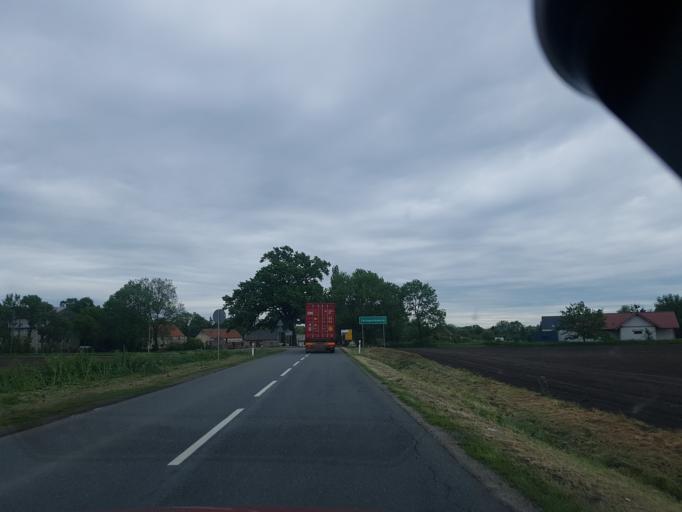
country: PL
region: Lower Silesian Voivodeship
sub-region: Powiat wroclawski
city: Kobierzyce
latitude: 50.9355
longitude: 16.9381
